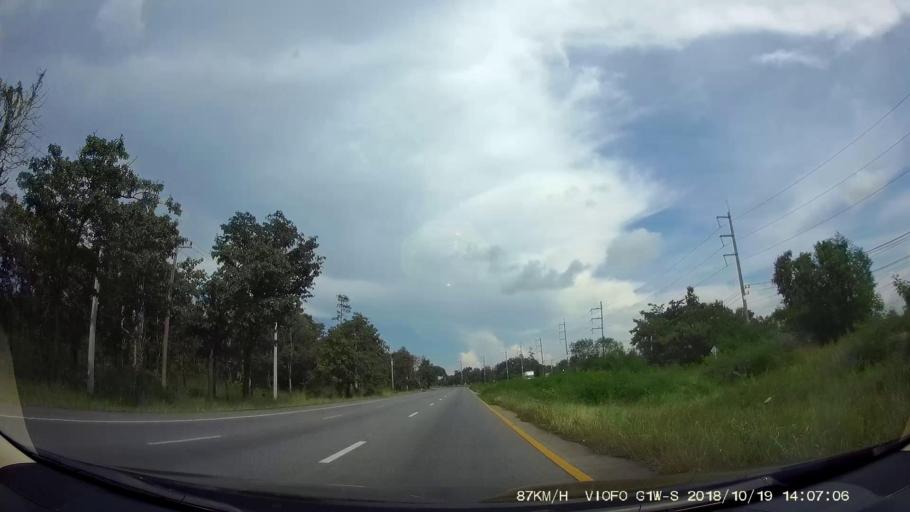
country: TH
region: Chaiyaphum
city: Chaiyaphum
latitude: 15.8916
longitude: 102.1127
